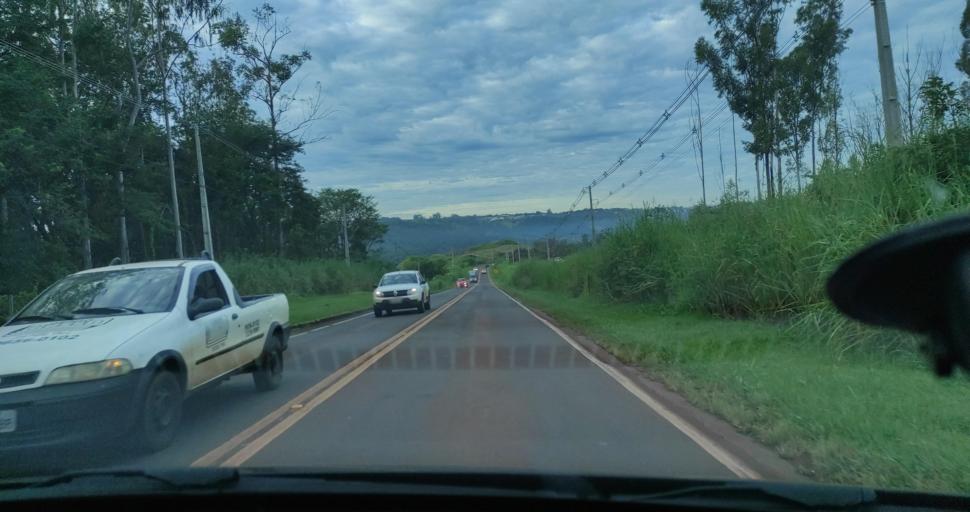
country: BR
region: Parana
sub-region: Ibipora
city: Ibipora
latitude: -23.2342
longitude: -51.0490
